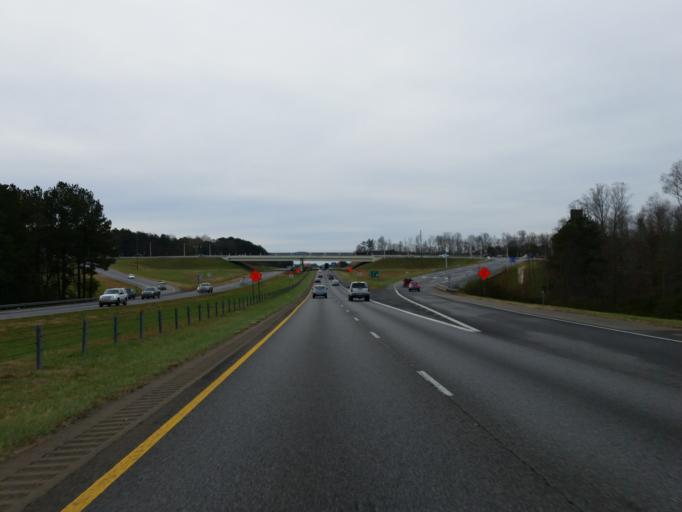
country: US
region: Georgia
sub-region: Cherokee County
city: Holly Springs
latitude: 34.1497
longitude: -84.5146
